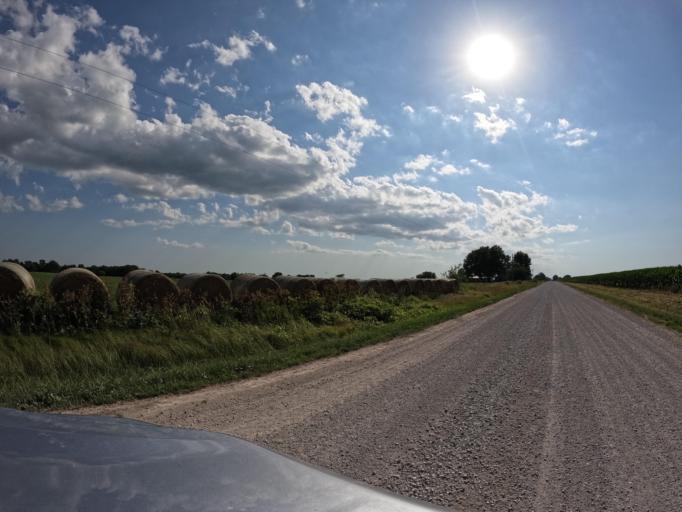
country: US
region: Iowa
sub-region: Appanoose County
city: Centerville
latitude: 40.7179
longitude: -93.0060
